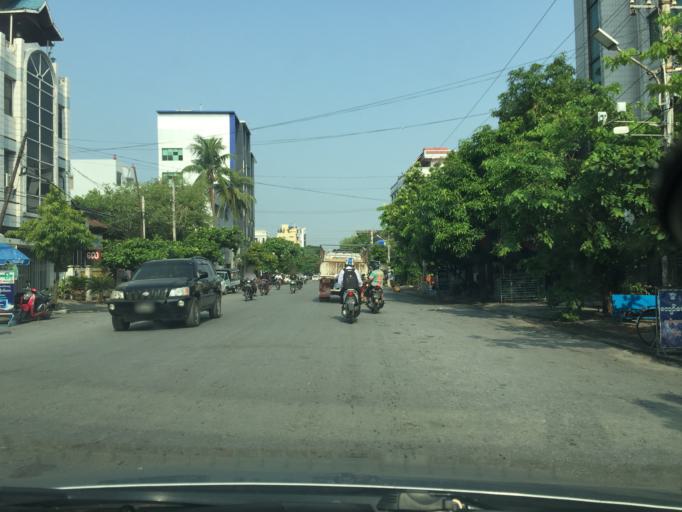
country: MM
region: Mandalay
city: Mandalay
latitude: 21.9711
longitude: 96.0798
